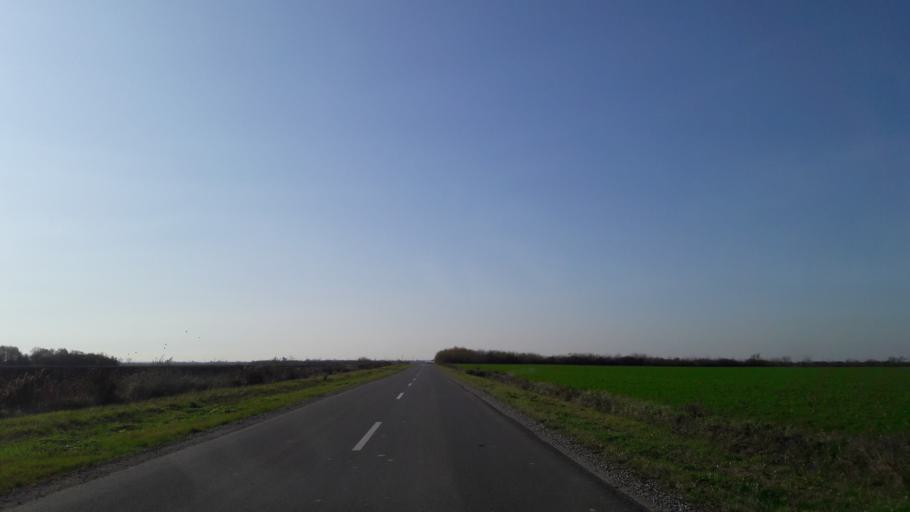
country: HR
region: Osjecko-Baranjska
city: Tenja
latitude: 45.4810
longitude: 18.7138
